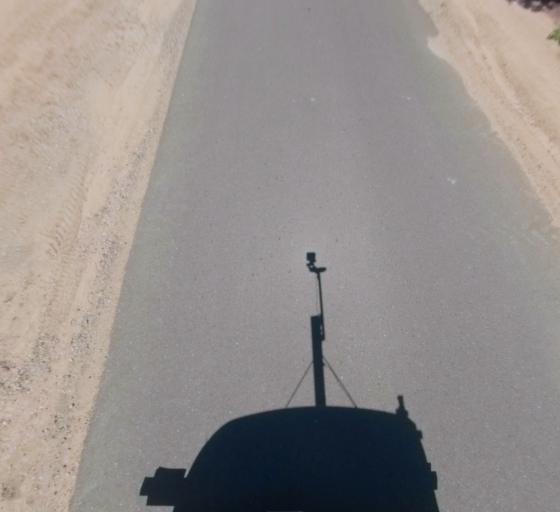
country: US
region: California
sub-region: Madera County
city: Bonadelle Ranchos-Madera Ranchos
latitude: 36.8951
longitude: -119.9276
